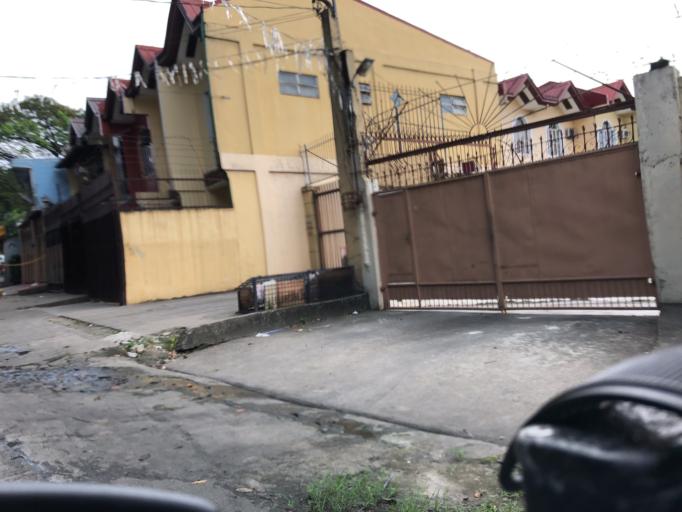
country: PH
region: Central Luzon
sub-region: Province of Bulacan
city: San Jose del Monte
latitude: 14.7432
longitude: 121.0599
